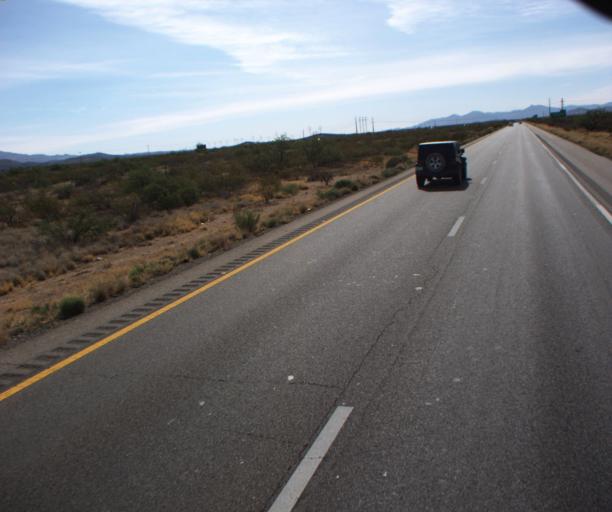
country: US
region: Arizona
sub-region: Pima County
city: Vail
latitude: 32.0398
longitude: -110.7399
